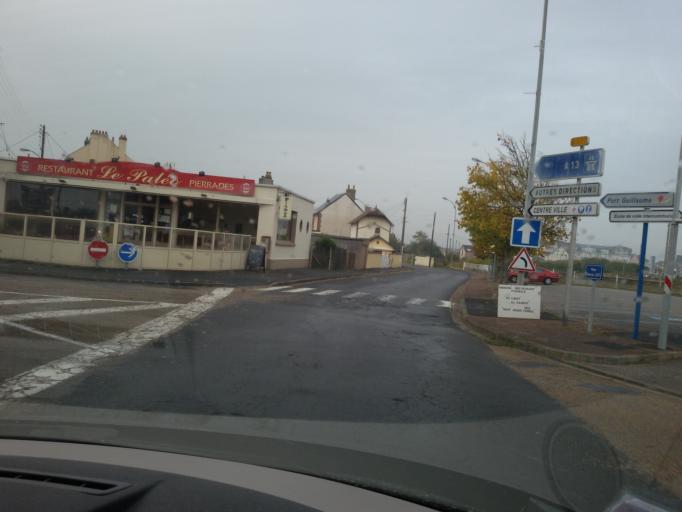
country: FR
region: Lower Normandy
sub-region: Departement du Calvados
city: Houlgate
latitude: 49.2943
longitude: -0.0906
